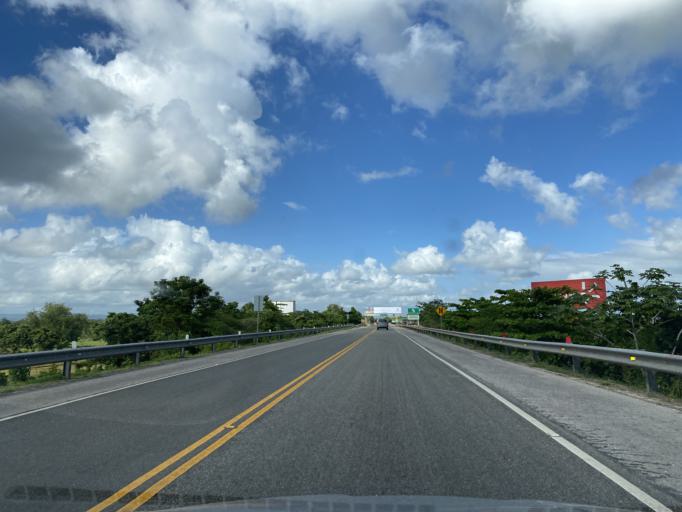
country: DO
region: Duarte
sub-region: Villa Riva
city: Agua Santa del Yuna
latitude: 19.1131
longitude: -69.8339
